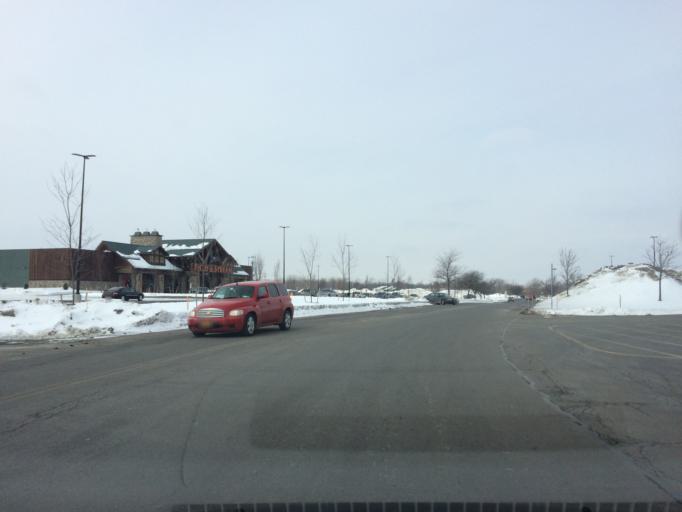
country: US
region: New York
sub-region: Monroe County
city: Rochester
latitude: 43.0808
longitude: -77.6343
